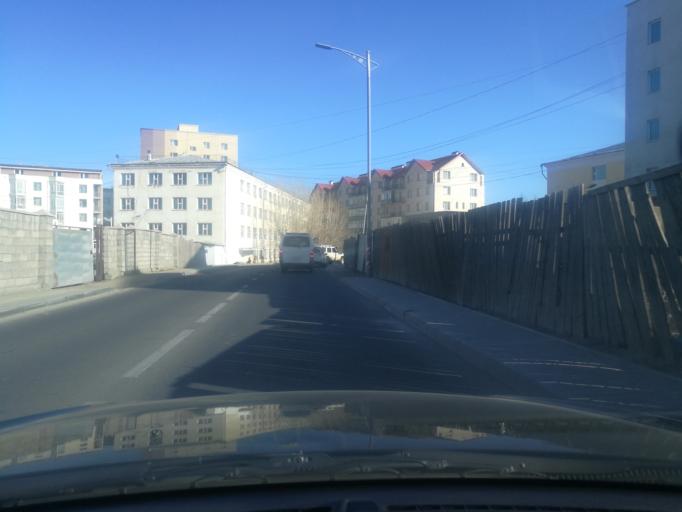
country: MN
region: Ulaanbaatar
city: Ulaanbaatar
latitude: 47.8867
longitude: 106.9050
